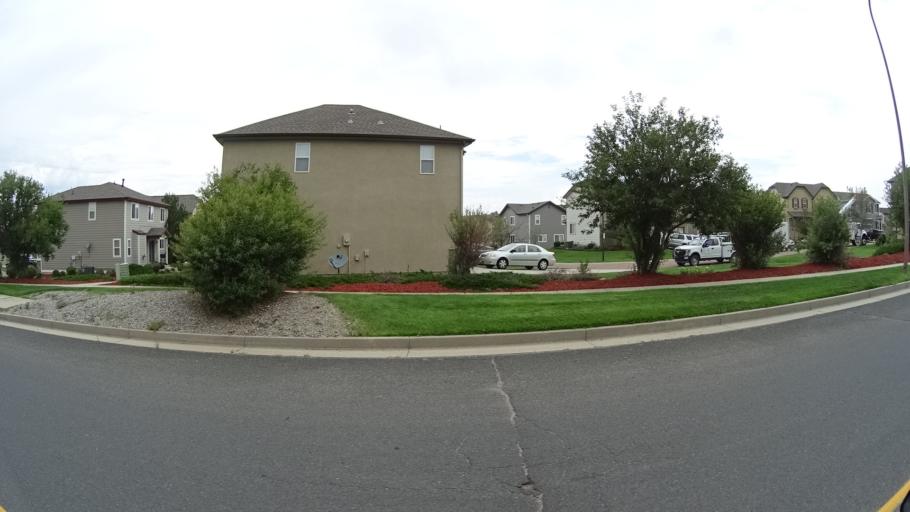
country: US
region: Colorado
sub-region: El Paso County
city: Gleneagle
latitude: 38.9980
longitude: -104.7947
